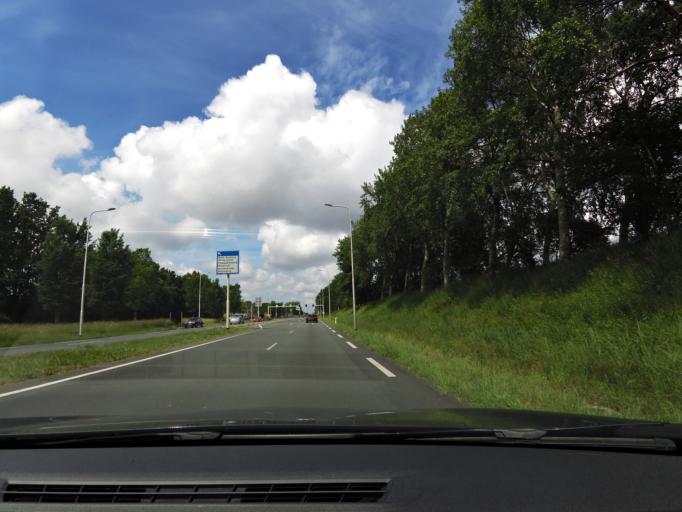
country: NL
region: Zeeland
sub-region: Gemeente Vlissingen
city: Vlissingen
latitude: 51.4615
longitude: 3.5915
